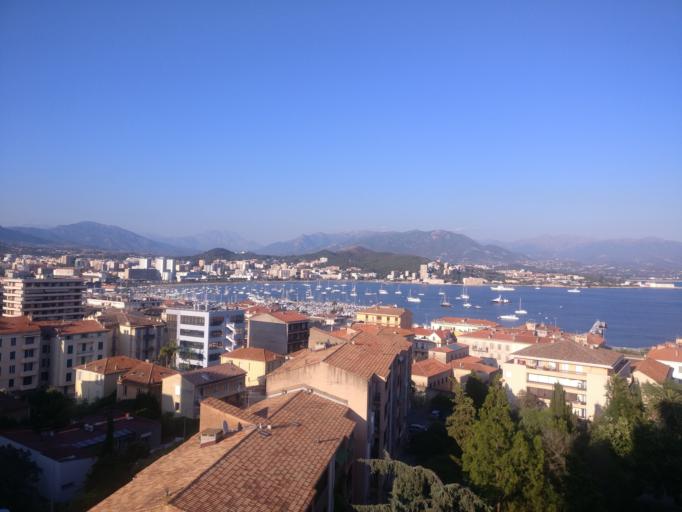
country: FR
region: Corsica
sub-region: Departement de la Corse-du-Sud
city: Ajaccio
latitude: 41.9256
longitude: 8.7348
